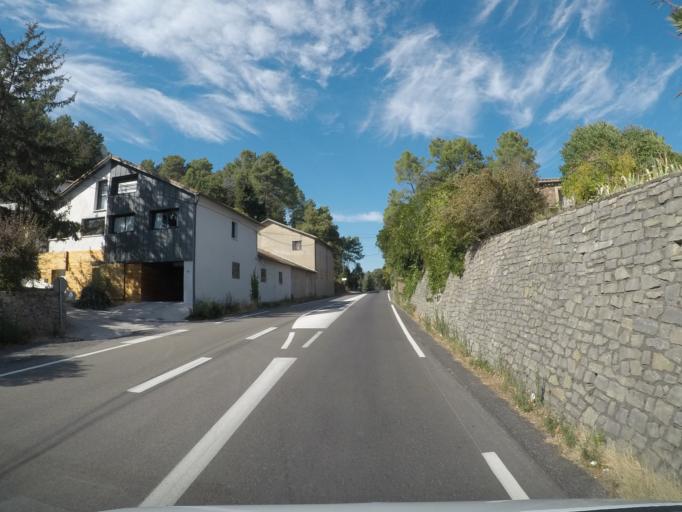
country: FR
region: Languedoc-Roussillon
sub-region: Departement du Gard
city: Anduze
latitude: 44.0714
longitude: 3.9689
